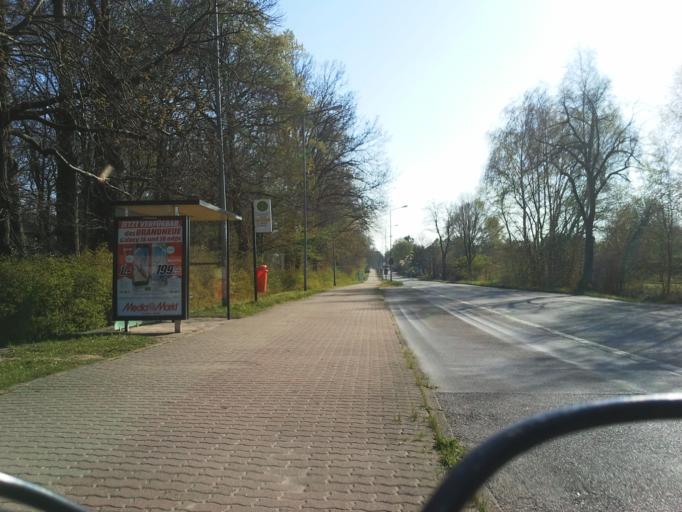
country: DE
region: Mecklenburg-Vorpommern
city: Rostock
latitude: 54.1021
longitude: 12.1306
